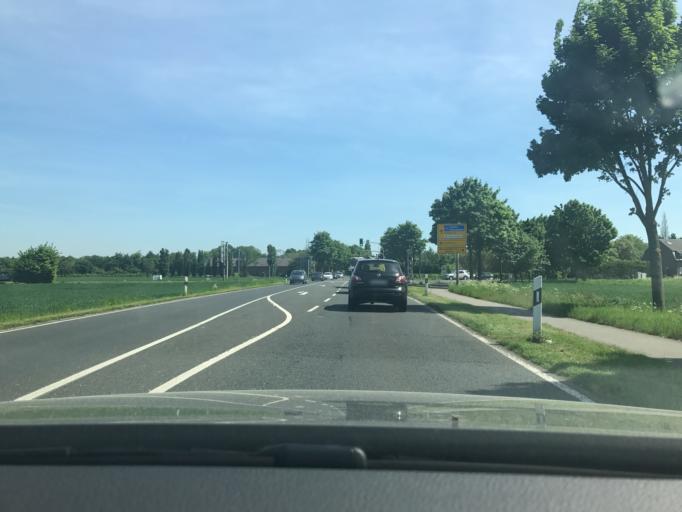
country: DE
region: North Rhine-Westphalia
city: Tonisvorst
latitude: 51.2754
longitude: 6.5020
